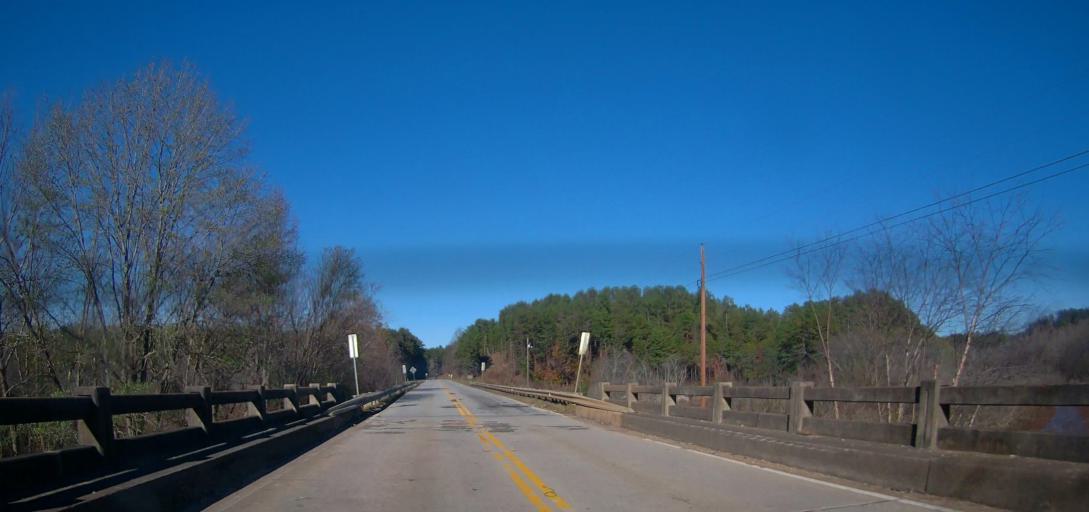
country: US
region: Georgia
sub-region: Hall County
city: Lula
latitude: 34.4140
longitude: -83.7088
